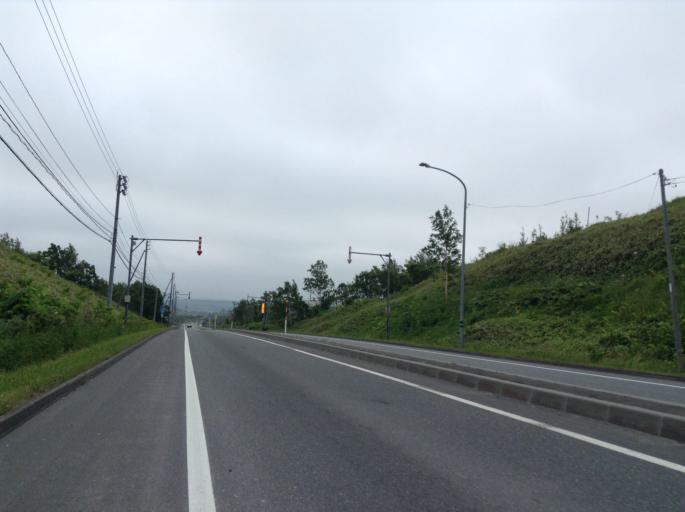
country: JP
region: Hokkaido
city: Wakkanai
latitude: 45.3732
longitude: 141.7175
